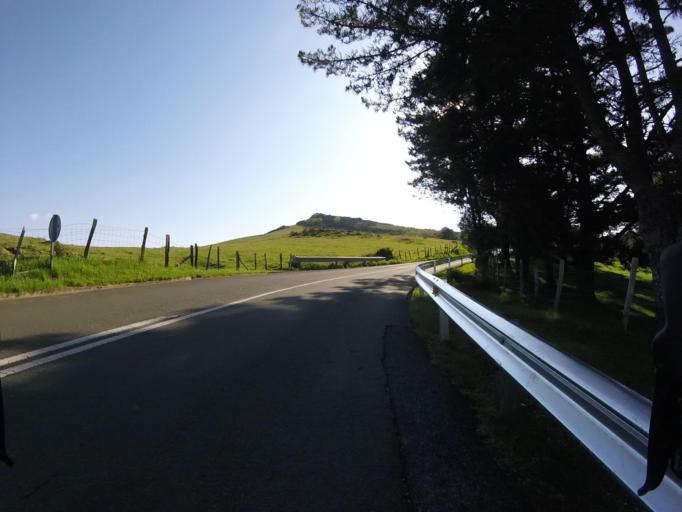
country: ES
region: Basque Country
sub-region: Provincia de Guipuzcoa
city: Fuenterrabia
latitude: 43.3504
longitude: -1.8464
